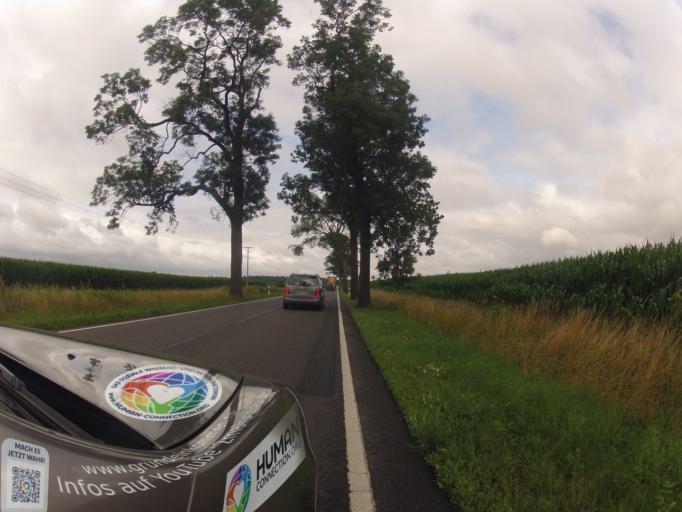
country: DE
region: Mecklenburg-Vorpommern
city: Anklam
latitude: 53.9042
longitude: 13.7535
